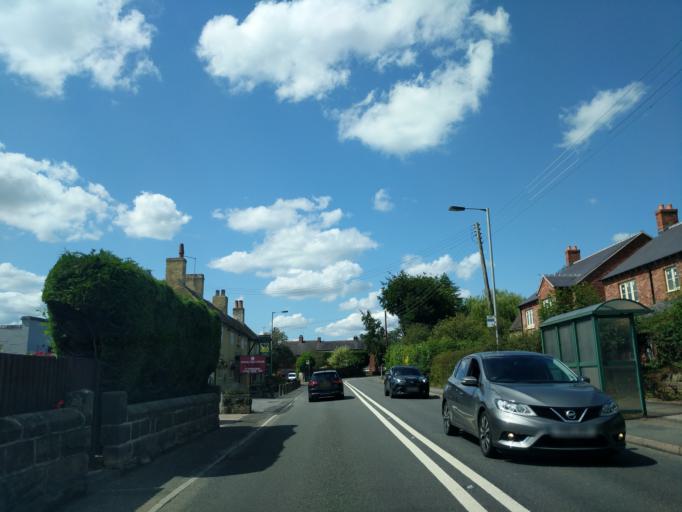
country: GB
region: England
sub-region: Staffordshire
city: Cheadle
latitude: 52.9447
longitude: -1.9771
